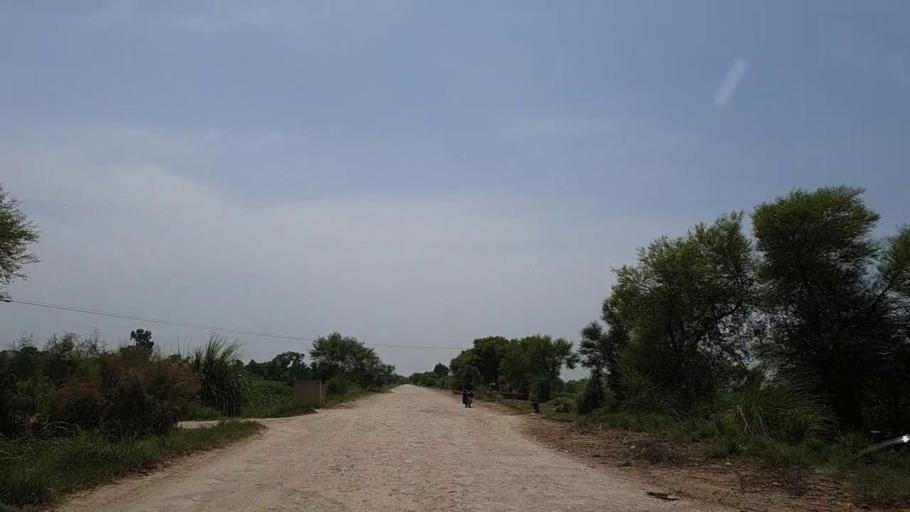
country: PK
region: Sindh
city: Khanpur
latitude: 27.8456
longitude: 69.4852
